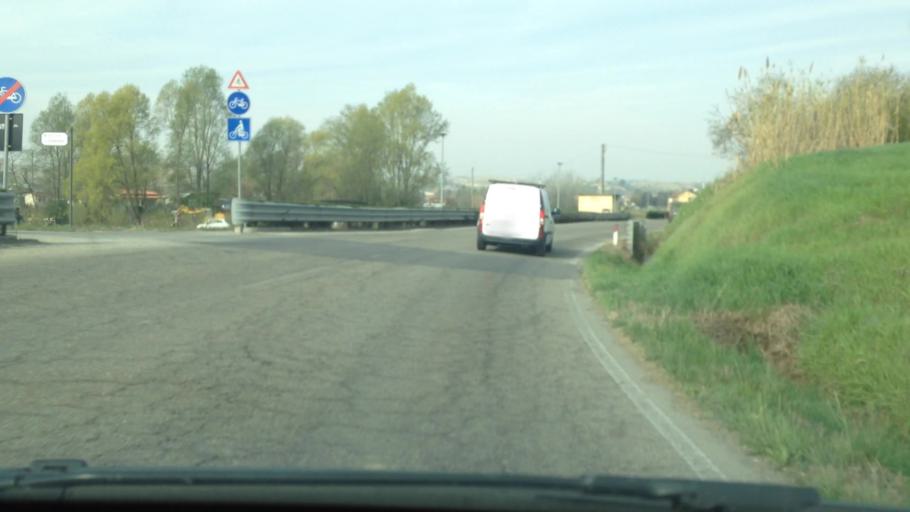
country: IT
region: Piedmont
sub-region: Provincia di Cuneo
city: Canale
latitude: 44.8002
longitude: 8.0148
